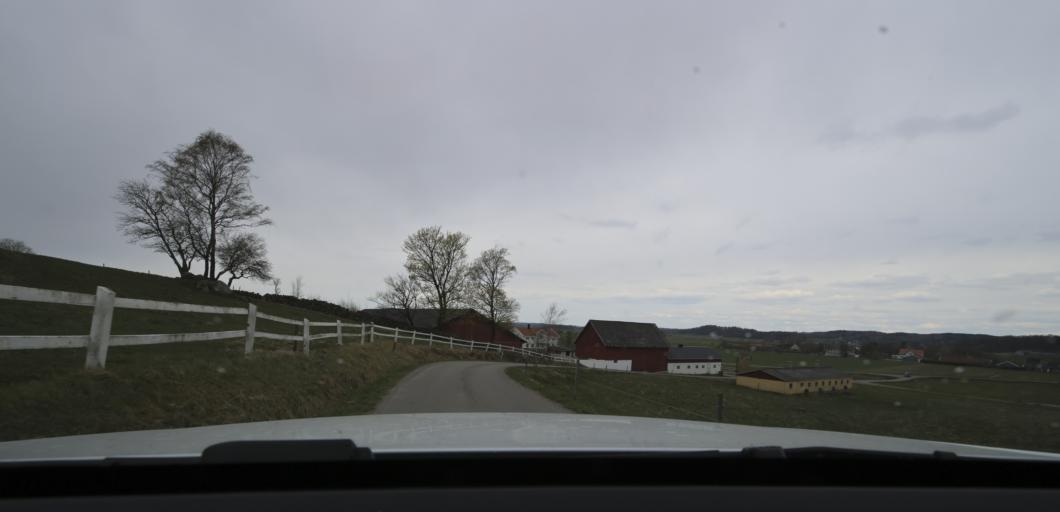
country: SE
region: Halland
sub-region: Varbergs Kommun
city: Tvaaker
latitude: 57.1298
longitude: 12.4565
